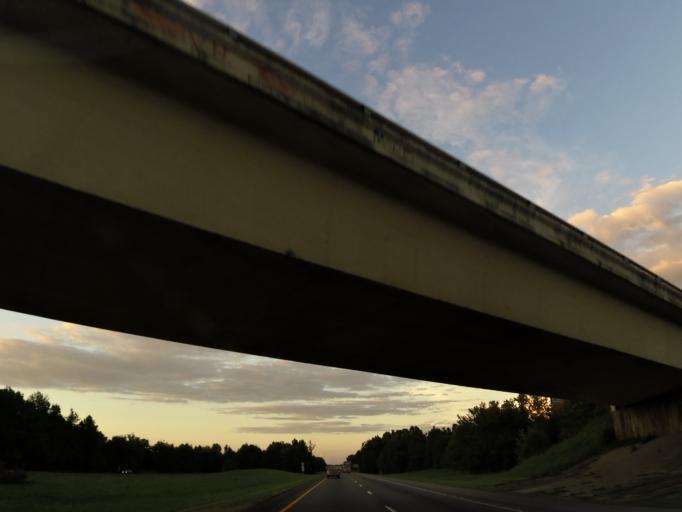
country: US
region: Tennessee
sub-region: Monroe County
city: Sweetwater
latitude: 35.5859
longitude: -84.5273
